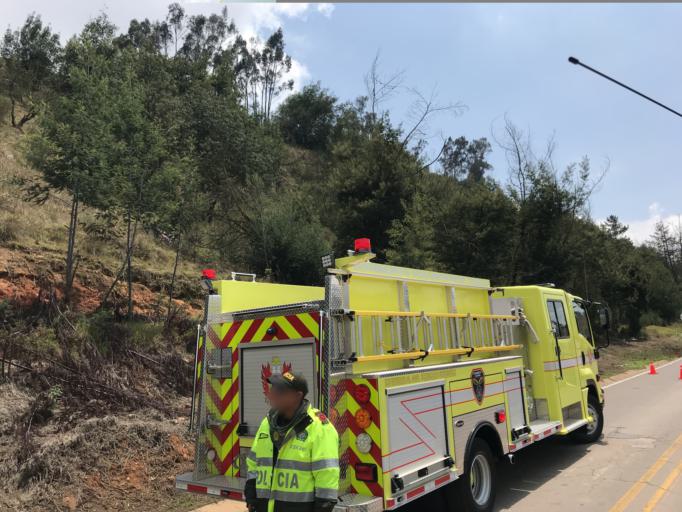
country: CO
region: Boyaca
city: Tunja
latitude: 5.5477
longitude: -73.3699
